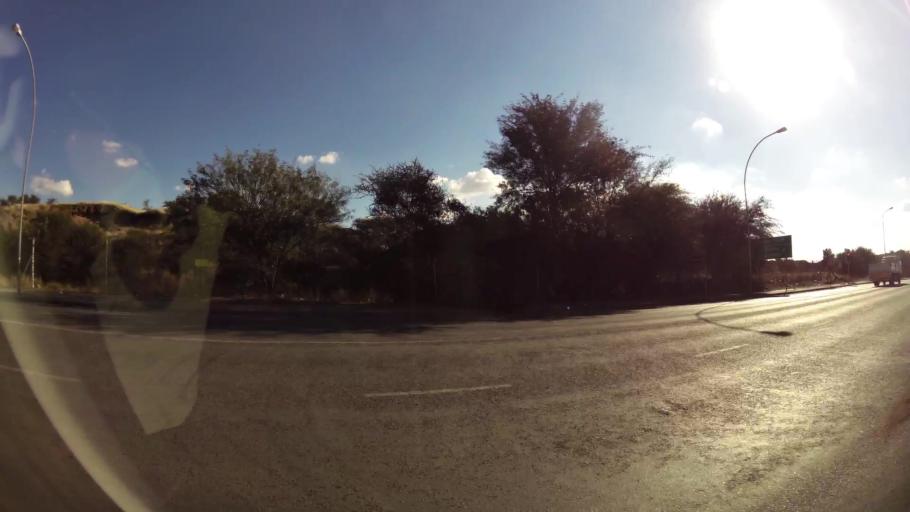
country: ZA
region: Northern Cape
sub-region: Frances Baard District Municipality
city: Kimberley
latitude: -28.7322
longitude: 24.7598
